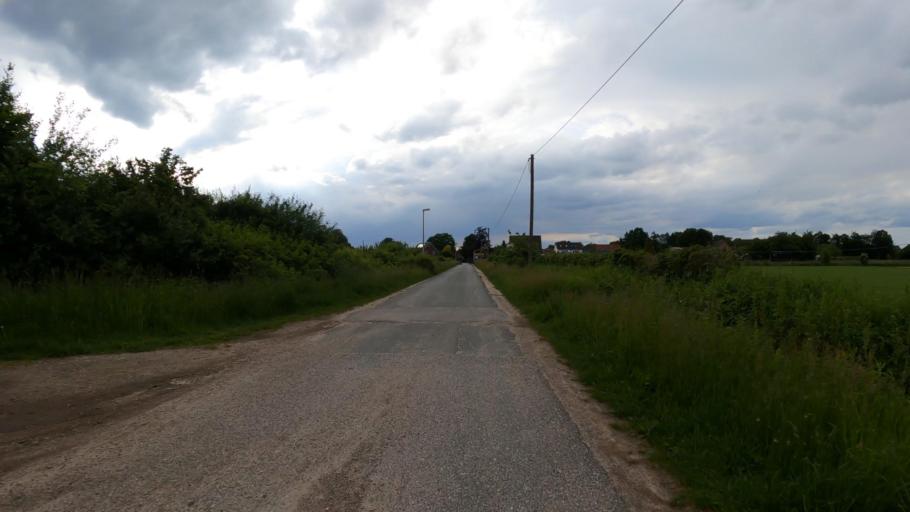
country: DE
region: Schleswig-Holstein
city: Appen
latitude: 53.6572
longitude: 9.7564
